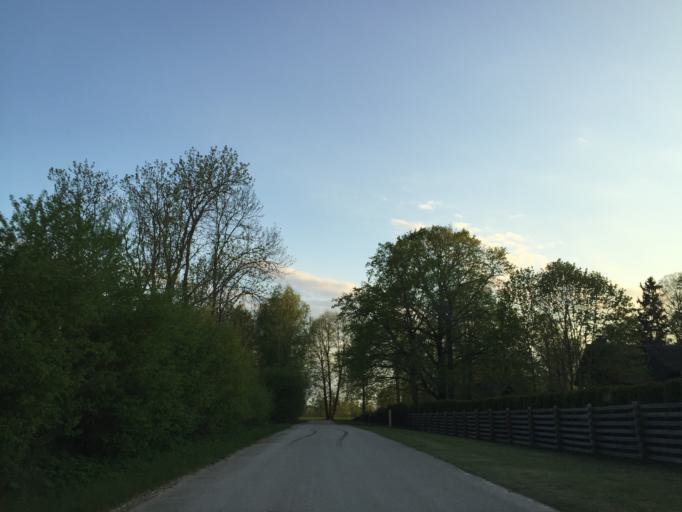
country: LV
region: Jurmala
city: Jurmala
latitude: 56.9042
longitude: 23.7368
